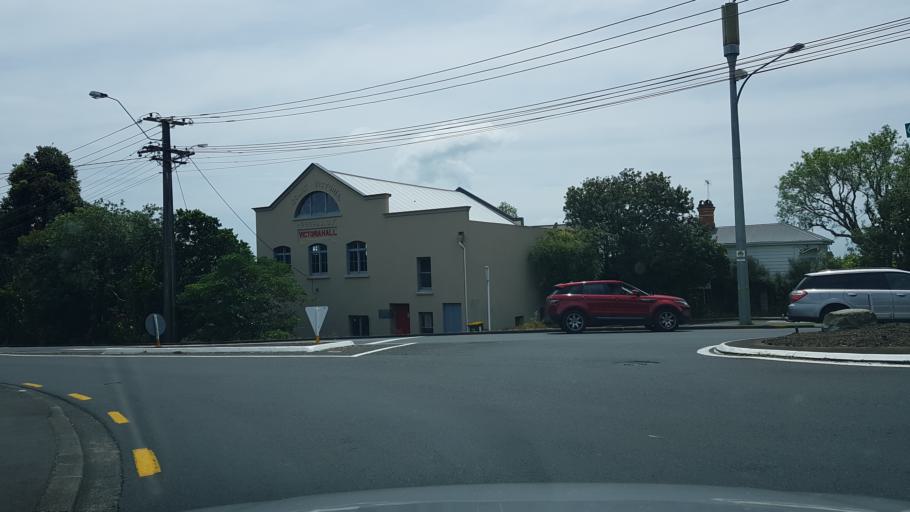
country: NZ
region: Auckland
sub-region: Auckland
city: Auckland
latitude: -36.8248
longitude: 174.7984
